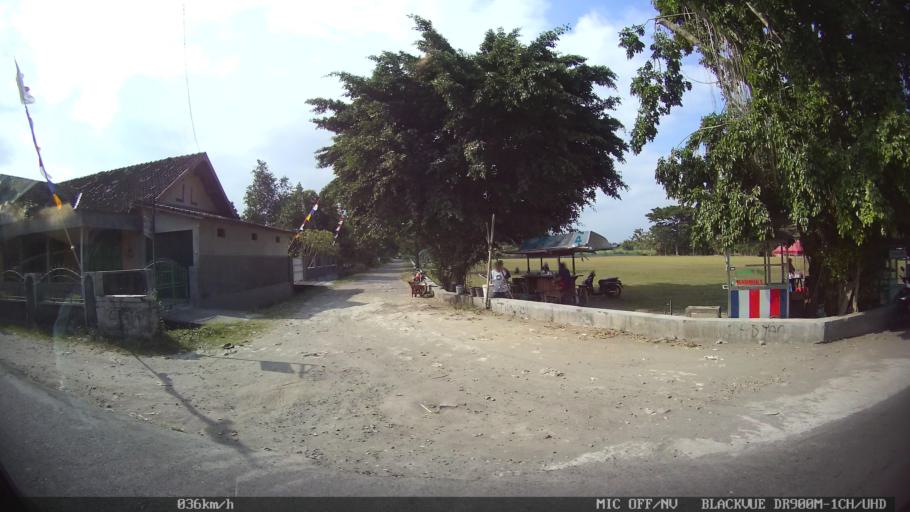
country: ID
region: Daerah Istimewa Yogyakarta
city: Sewon
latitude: -7.8708
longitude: 110.3607
